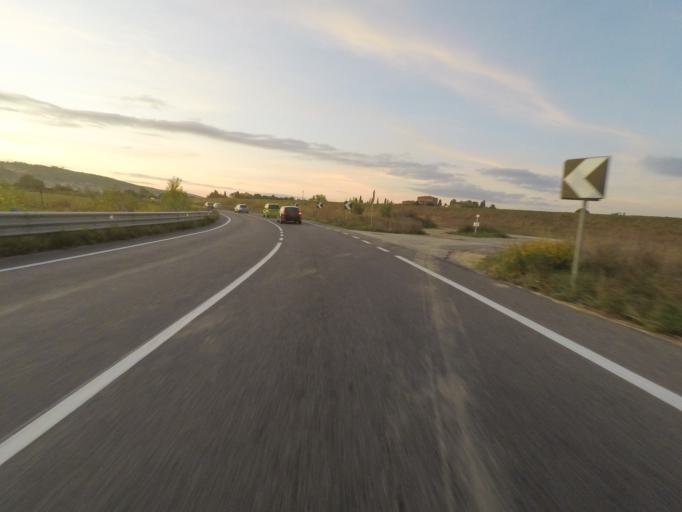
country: IT
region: Tuscany
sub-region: Provincia di Siena
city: Guazzino
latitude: 43.2048
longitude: 11.7657
